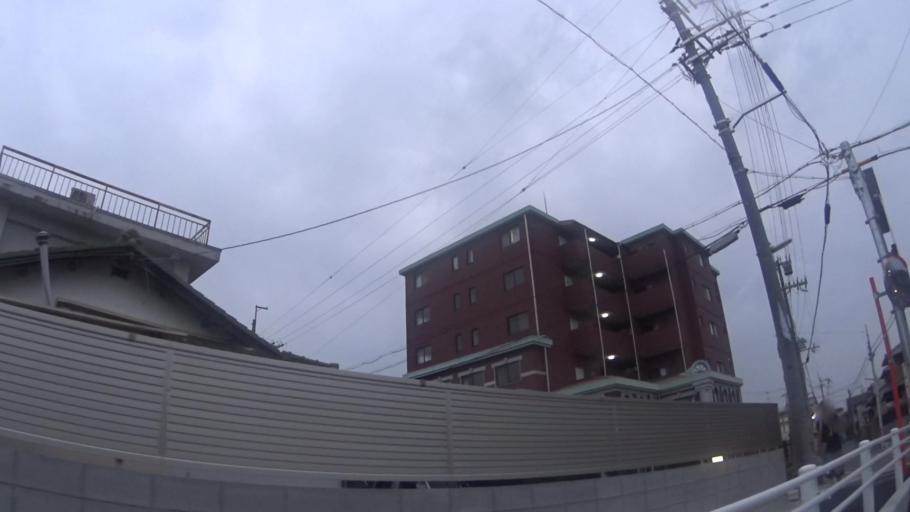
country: JP
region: Kyoto
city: Muko
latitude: 34.9475
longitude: 135.7084
